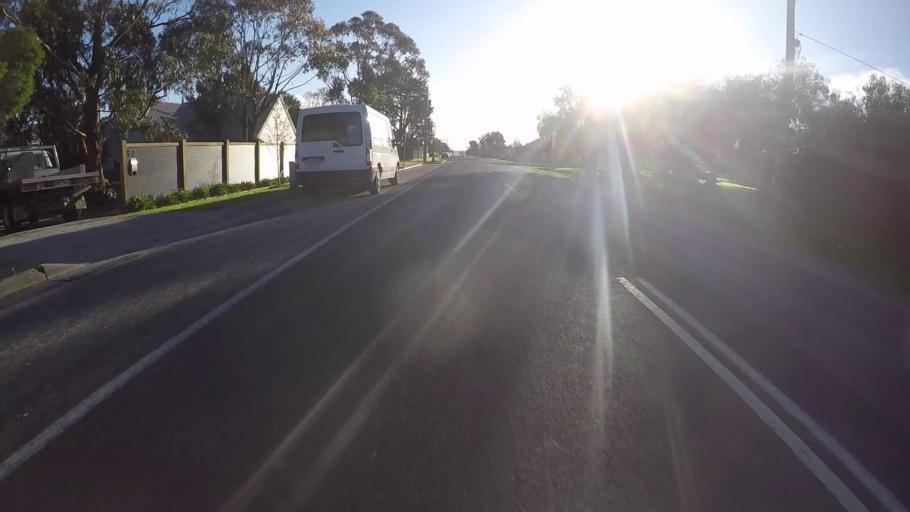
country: AU
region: Victoria
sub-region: Greater Geelong
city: Wandana Heights
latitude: -38.1710
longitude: 144.2770
